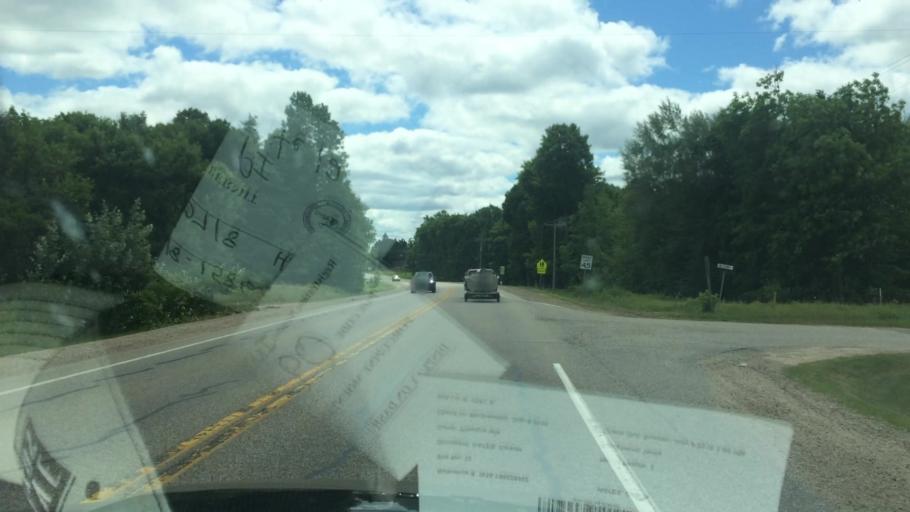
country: US
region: Wisconsin
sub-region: Vilas County
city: Eagle River
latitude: 45.7938
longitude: -89.3209
